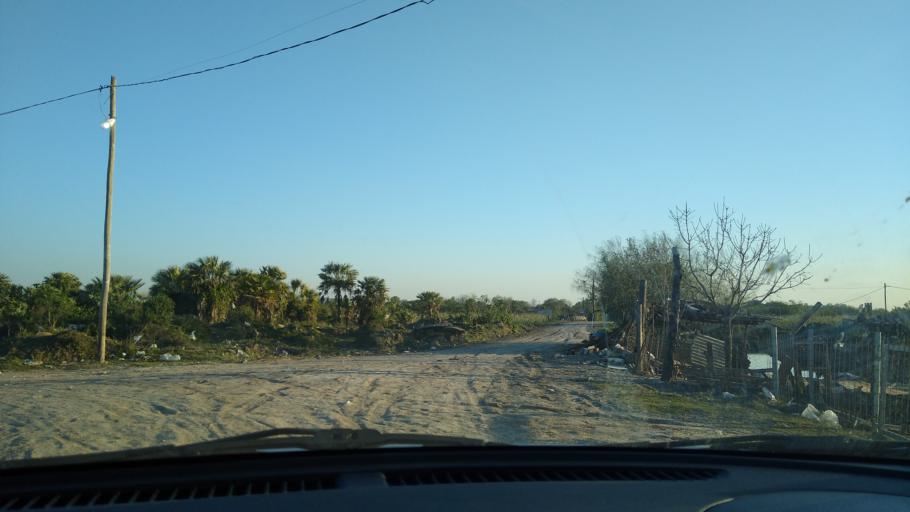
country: AR
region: Chaco
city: Puerto Vilelas
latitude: -27.5053
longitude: -58.9544
